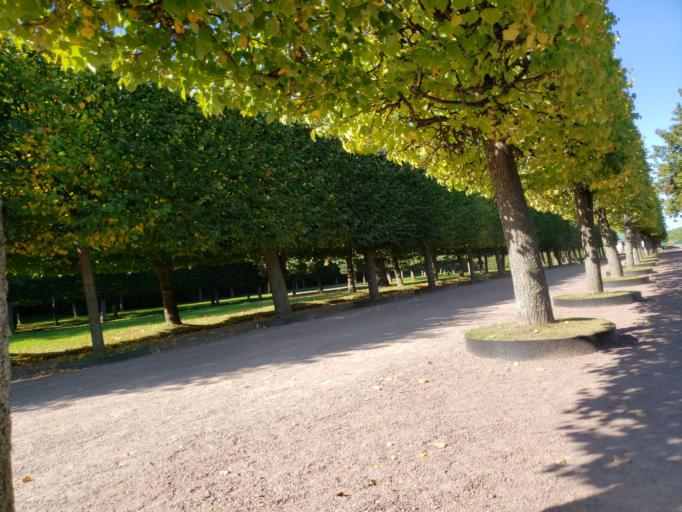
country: RU
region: St.-Petersburg
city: Peterhof
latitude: 59.8884
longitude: 29.8958
